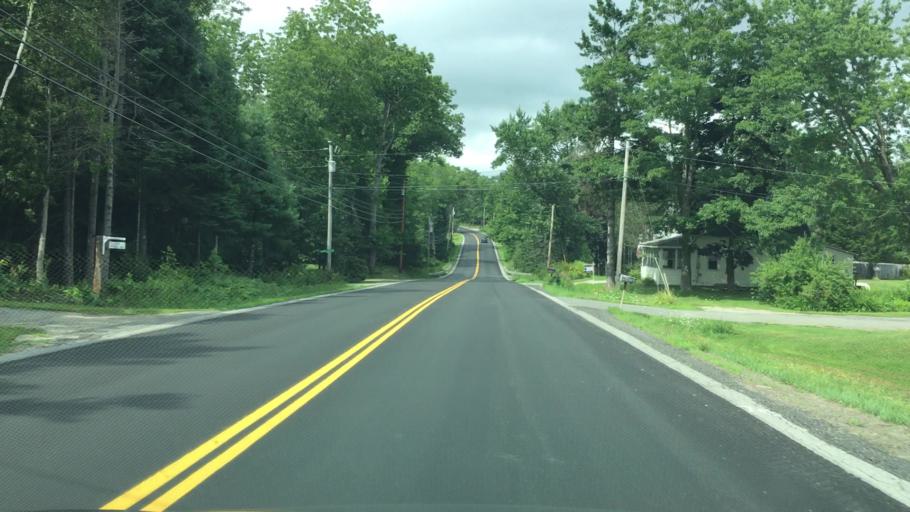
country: US
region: Maine
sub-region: Hancock County
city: Bucksport
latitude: 44.6007
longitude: -68.8156
